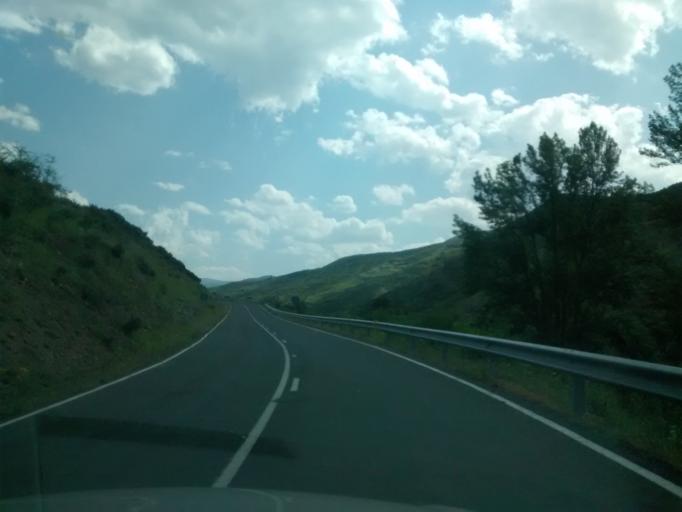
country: ES
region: La Rioja
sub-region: Provincia de La Rioja
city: Jalon de Cameros
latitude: 42.2133
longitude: -2.4774
